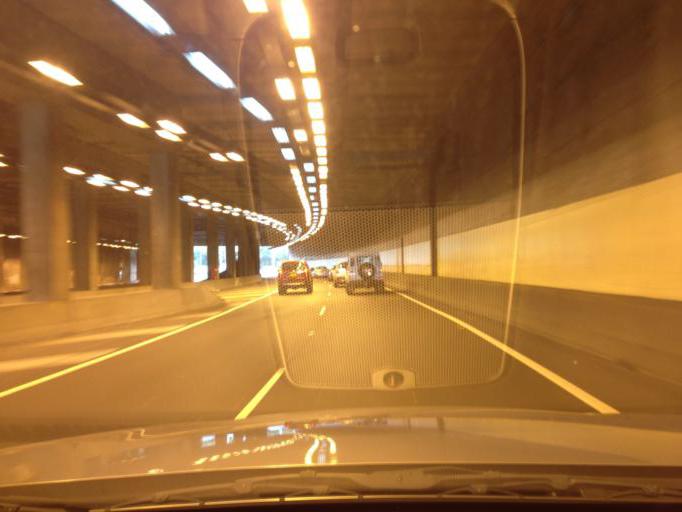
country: AU
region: New South Wales
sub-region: City of Sydney
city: Darlinghurst
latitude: -33.8686
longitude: 151.2182
